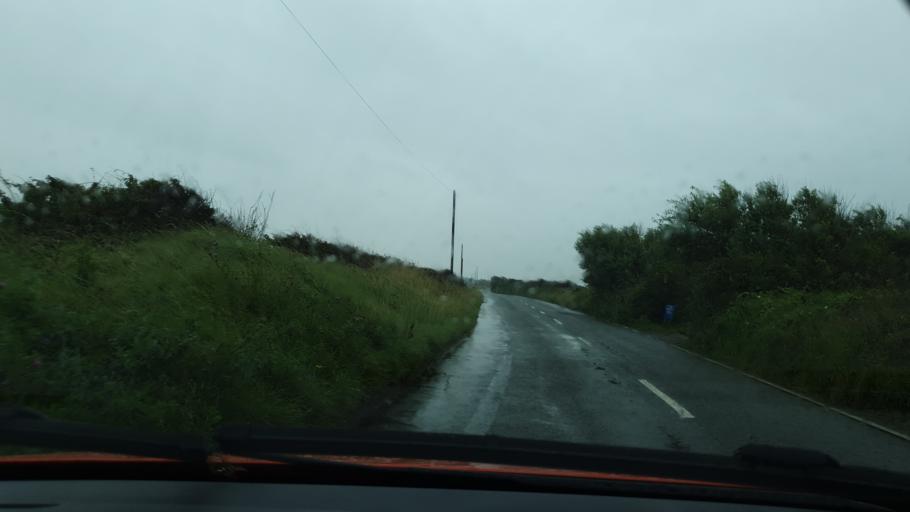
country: GB
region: England
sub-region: Cumbria
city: Barrow in Furness
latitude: 54.0907
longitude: -3.2461
